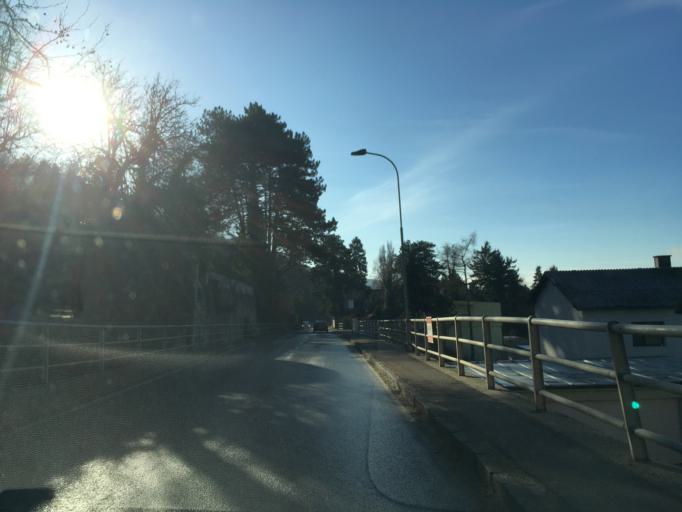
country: AT
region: Lower Austria
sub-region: Politischer Bezirk Tulln
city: Wordern
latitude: 48.3399
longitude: 16.2328
